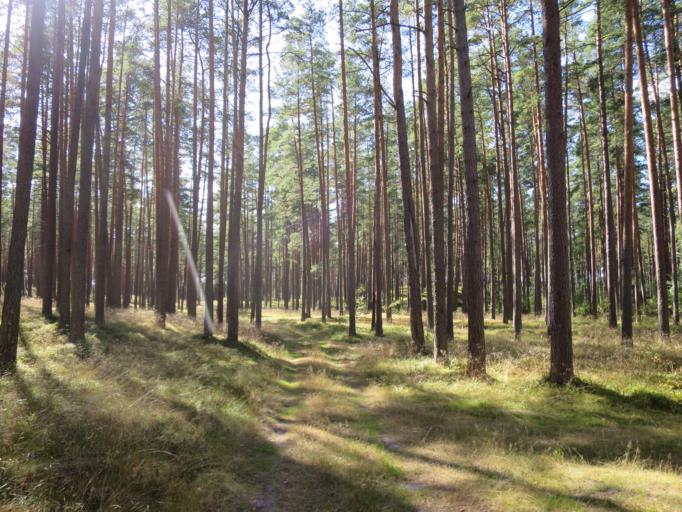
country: LV
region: Riga
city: Jaunciems
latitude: 57.0627
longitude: 24.2287
